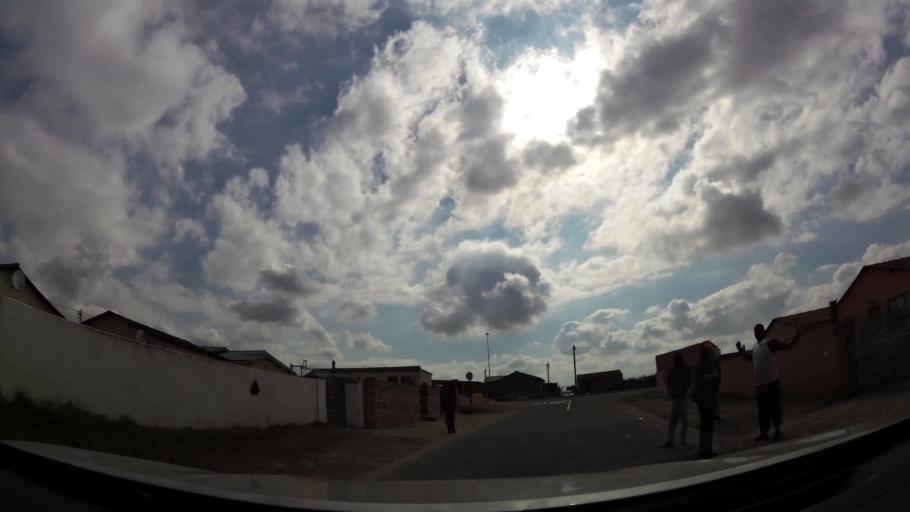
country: ZA
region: Eastern Cape
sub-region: Nelson Mandela Bay Metropolitan Municipality
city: Port Elizabeth
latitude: -33.8080
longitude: 25.5864
